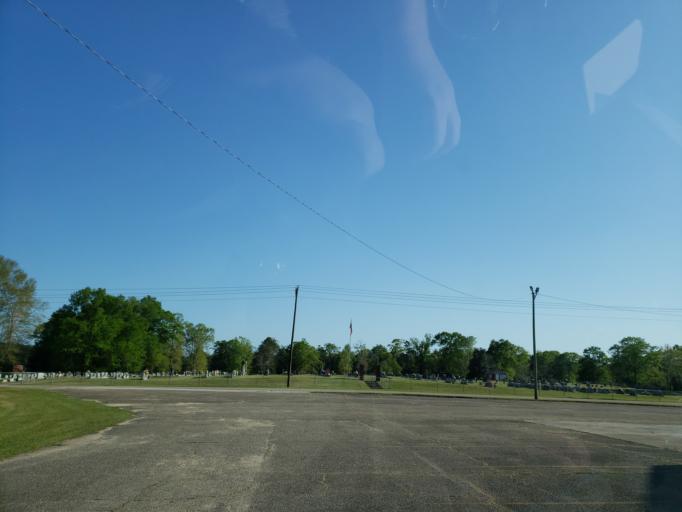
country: US
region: Mississippi
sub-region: Jones County
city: Ellisville
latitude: 31.6782
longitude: -89.3085
